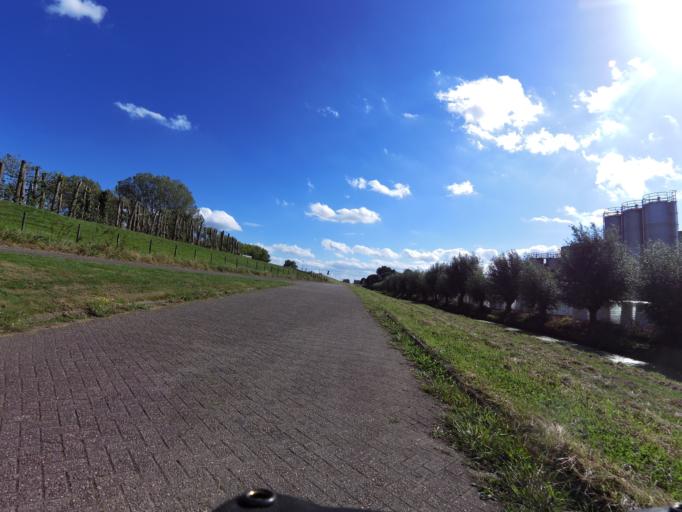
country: NL
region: South Holland
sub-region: Gemeente Zwijndrecht
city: Zwijndrecht
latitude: 51.7851
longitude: 4.6221
